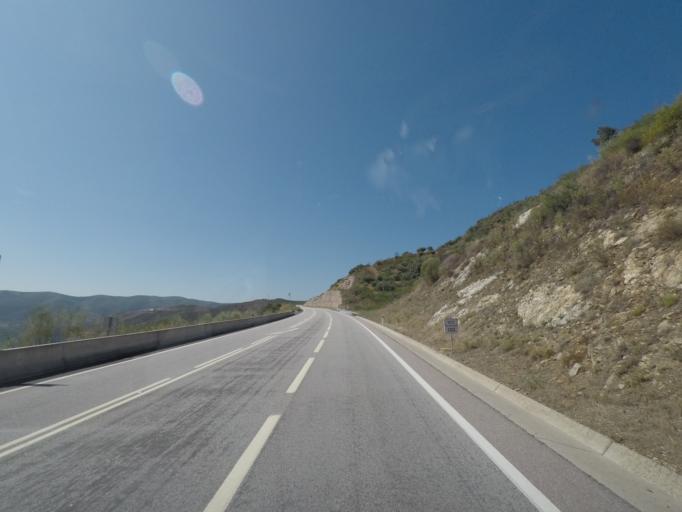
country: PT
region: Braganca
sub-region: Alfandega da Fe
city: Alfandega da Fe
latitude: 41.2825
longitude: -6.8801
